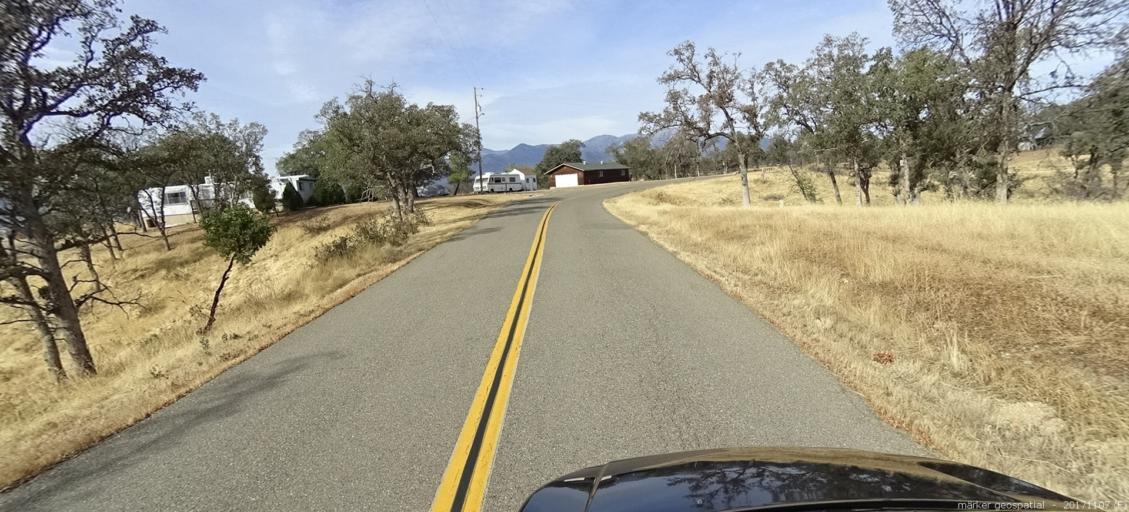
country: US
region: California
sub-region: Shasta County
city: Shasta
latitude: 40.4517
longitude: -122.5326
